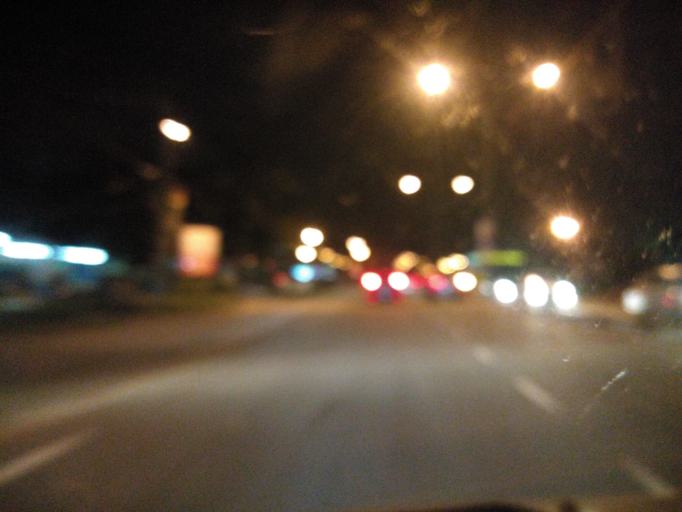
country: MY
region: Penang
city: Butterworth
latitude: 5.4000
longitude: 100.3758
